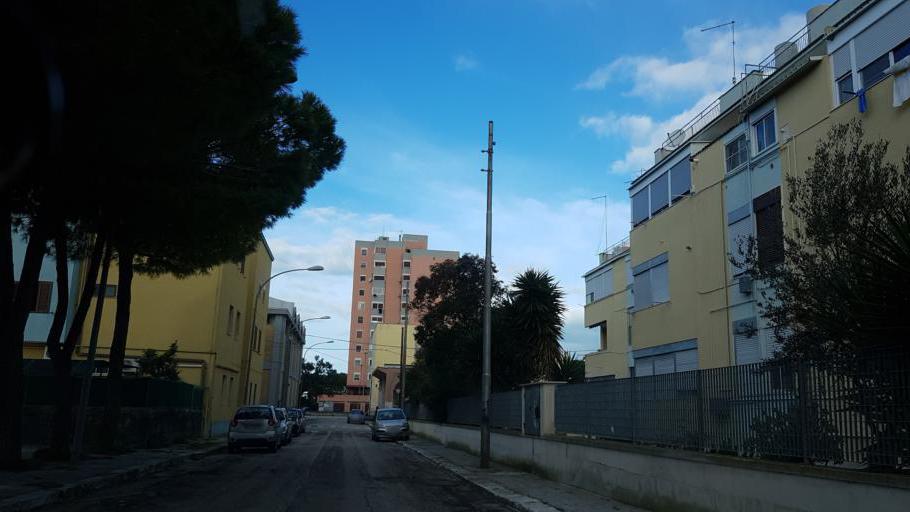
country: IT
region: Apulia
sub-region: Provincia di Brindisi
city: Brindisi
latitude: 40.6311
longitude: 17.9538
